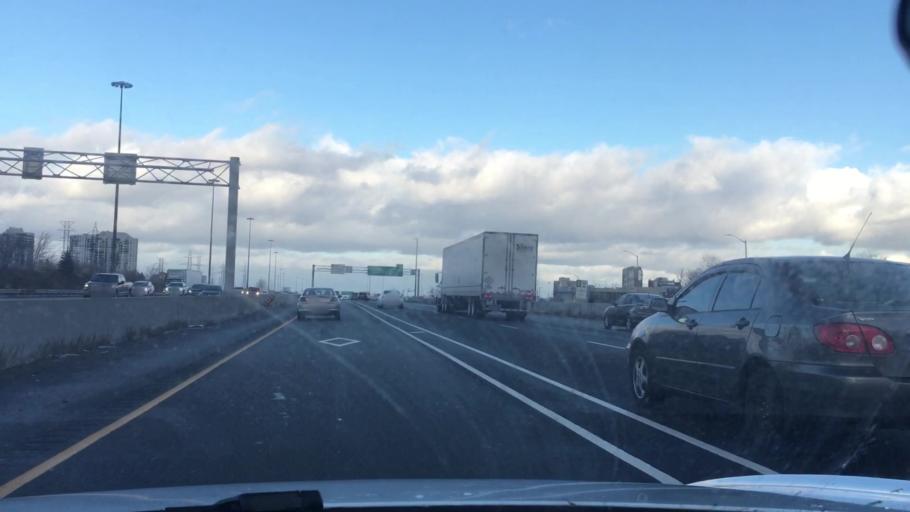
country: CA
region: Ontario
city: Mississauga
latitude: 43.5920
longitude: -79.6522
